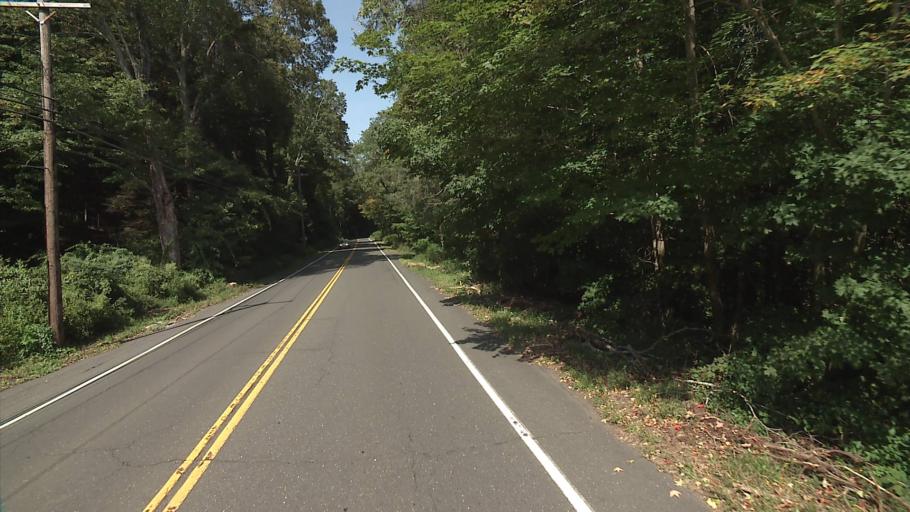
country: US
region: Connecticut
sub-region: Fairfield County
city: Georgetown
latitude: 41.2559
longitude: -73.3239
